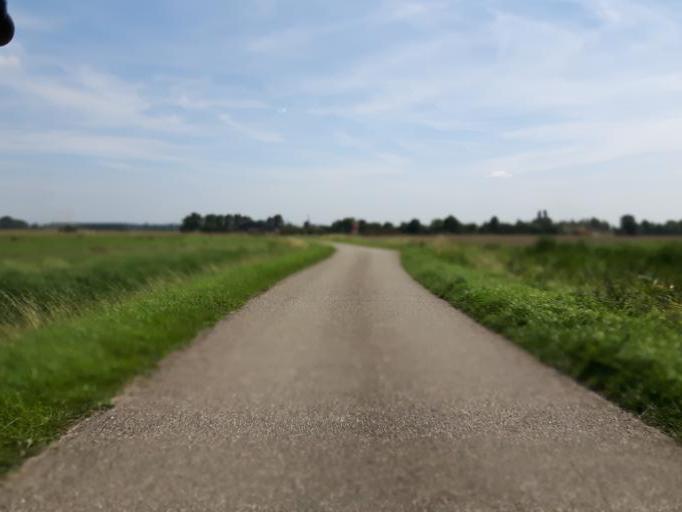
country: NL
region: Zeeland
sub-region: Gemeente Goes
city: Goes
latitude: 51.4646
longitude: 3.8515
